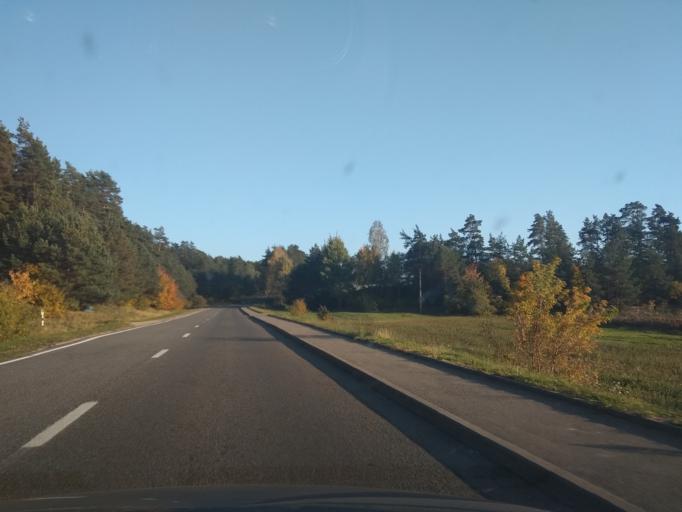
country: BY
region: Grodnenskaya
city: Vawkavysk
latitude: 53.1554
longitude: 24.4920
